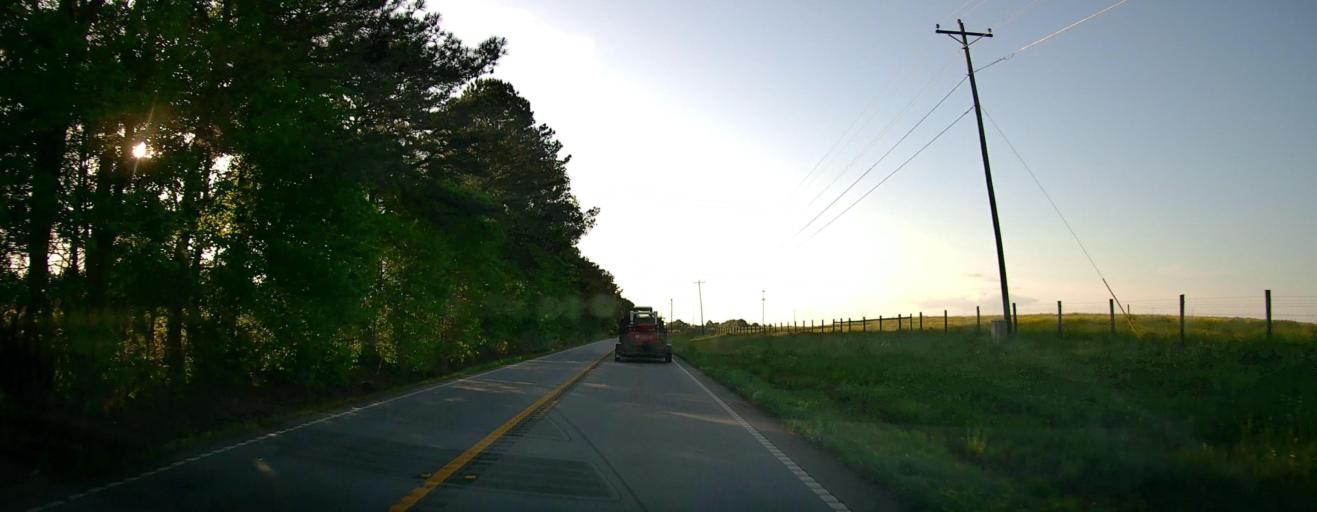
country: US
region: Georgia
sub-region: Walton County
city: Social Circle
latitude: 33.5472
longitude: -83.7321
